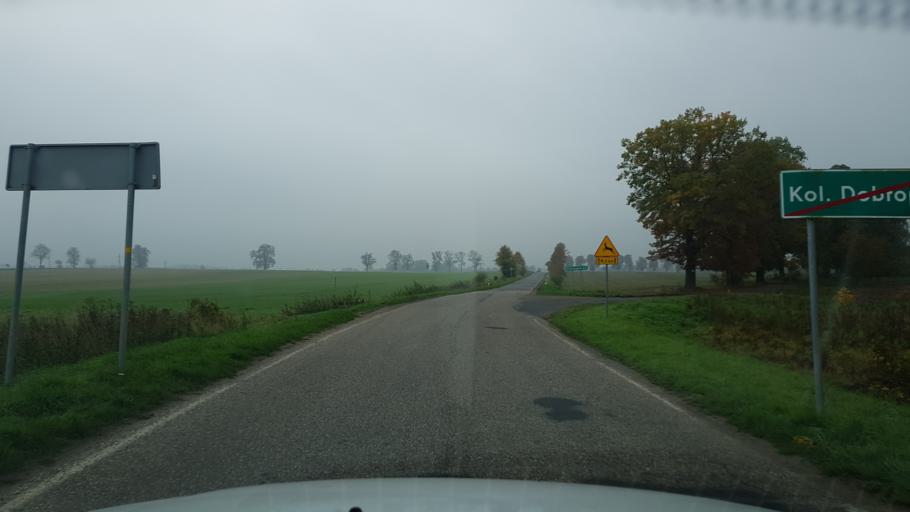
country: PL
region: West Pomeranian Voivodeship
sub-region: Powiat stargardzki
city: Dolice
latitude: 53.1560
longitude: 15.2400
